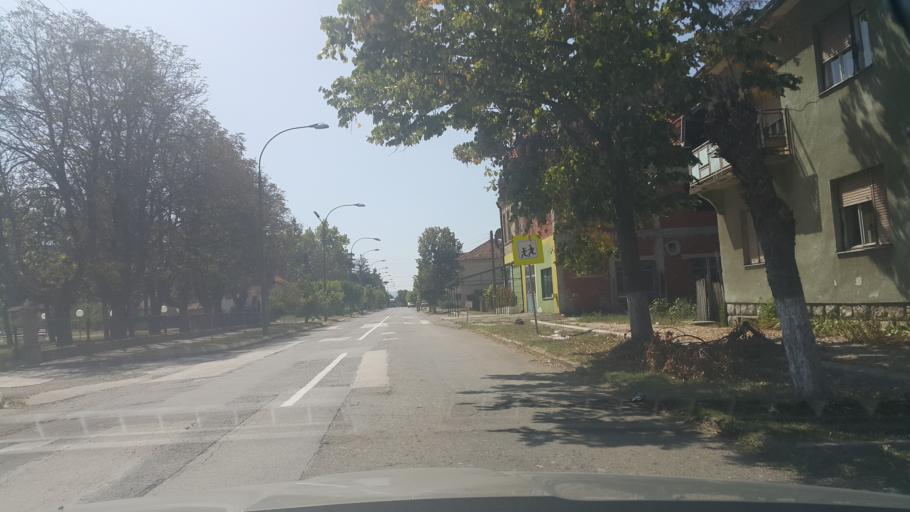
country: RS
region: Central Serbia
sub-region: Zajecarski Okrug
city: Knjazevac
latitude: 43.6869
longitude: 22.2934
